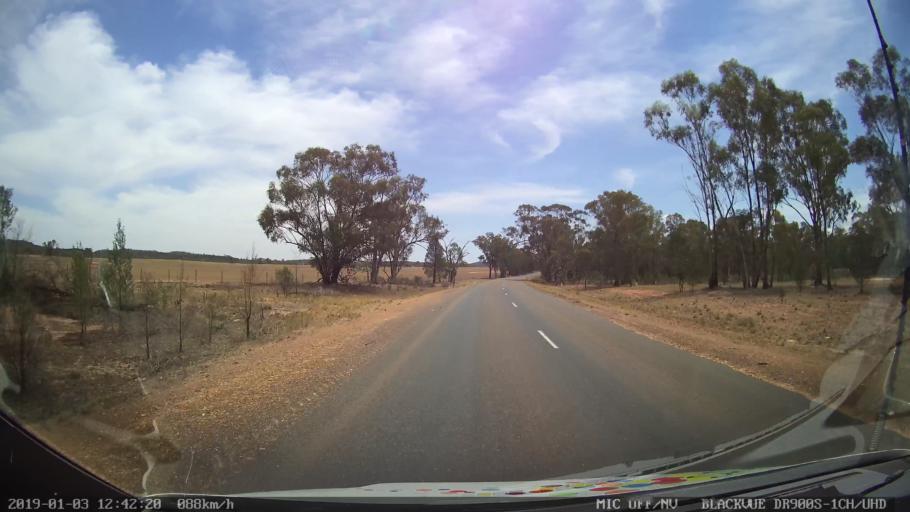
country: AU
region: New South Wales
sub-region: Weddin
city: Grenfell
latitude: -33.7887
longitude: 148.2115
